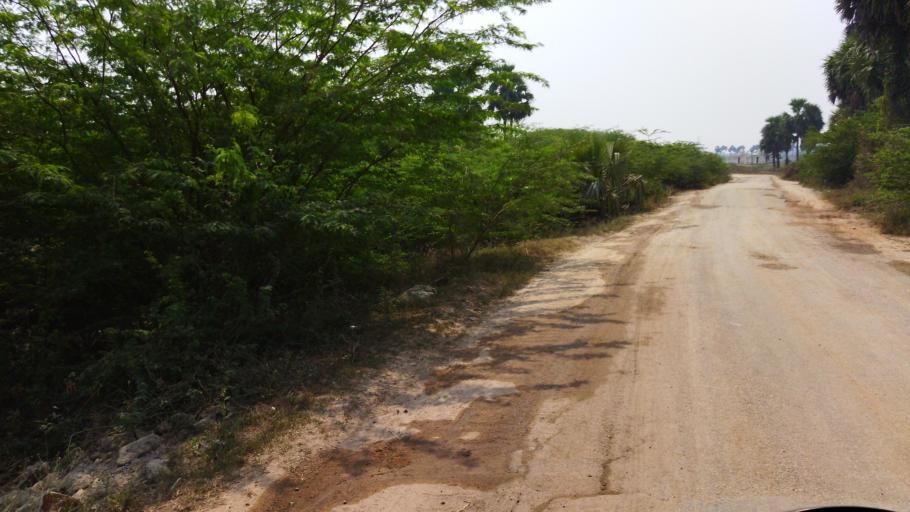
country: IN
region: Telangana
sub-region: Nalgonda
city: Nalgonda
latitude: 17.1401
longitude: 79.3864
